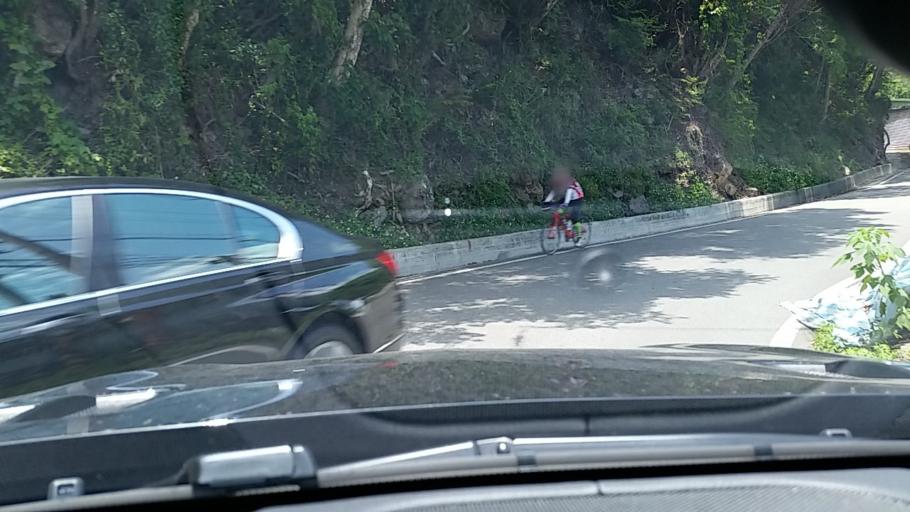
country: TW
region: Taiwan
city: Daxi
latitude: 24.6943
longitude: 121.3740
